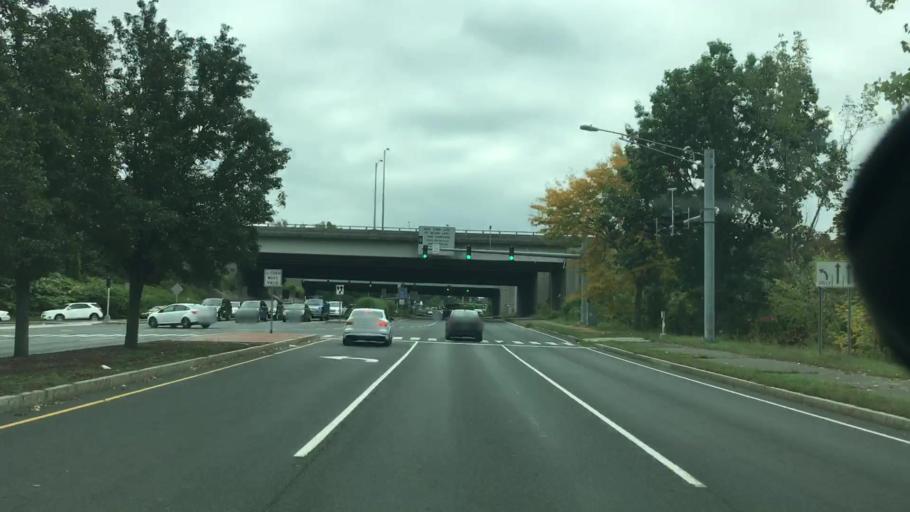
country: US
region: Connecticut
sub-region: Hartford County
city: Manchester
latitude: 41.8033
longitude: -72.5533
